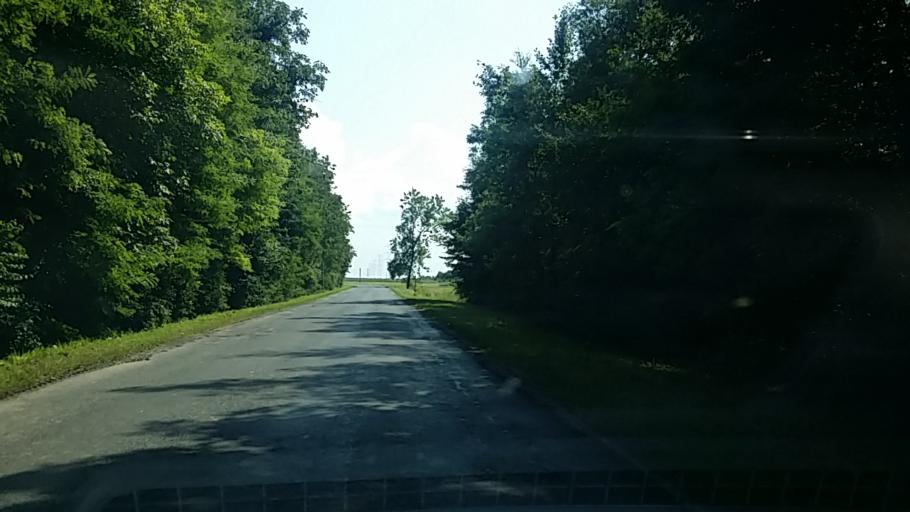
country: HU
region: Zala
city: Lenti
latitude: 46.5531
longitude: 16.5920
